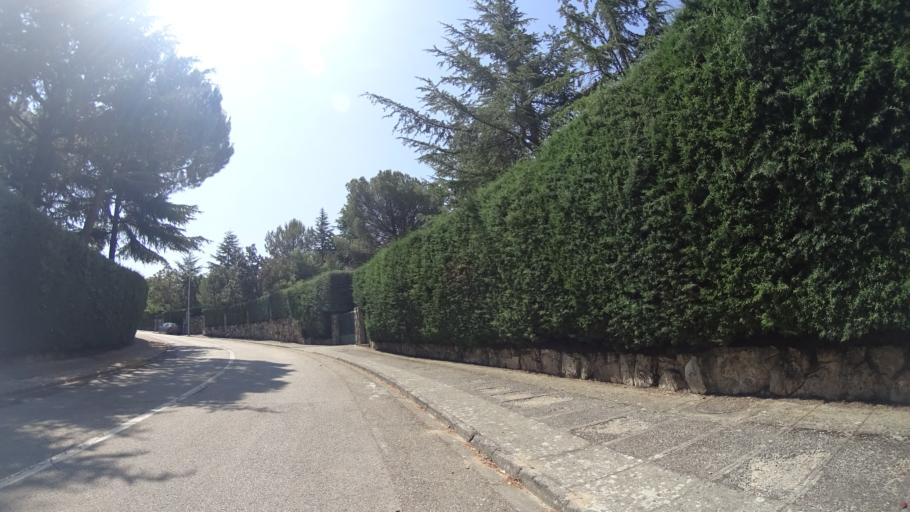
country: ES
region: Madrid
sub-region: Provincia de Madrid
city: Torrelodones
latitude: 40.6003
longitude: -3.9429
